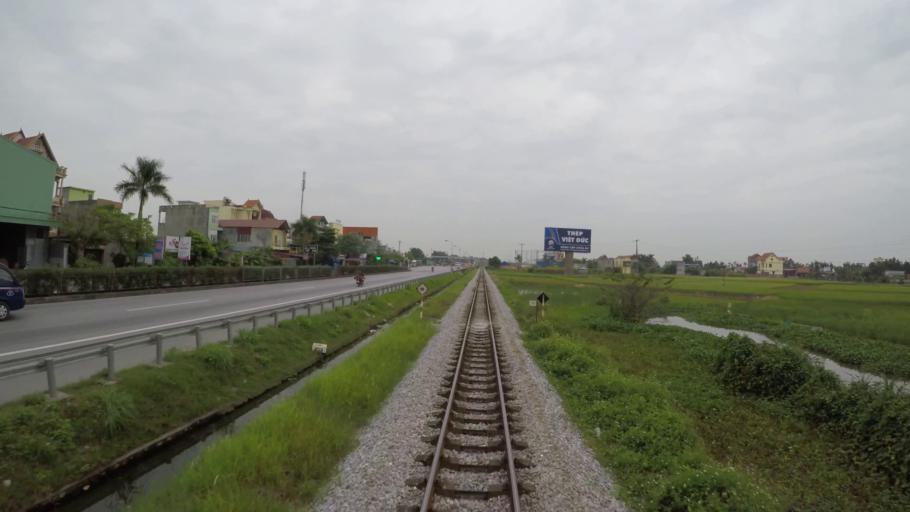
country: VN
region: Hai Duong
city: Phu Thai
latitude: 20.9281
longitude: 106.5556
